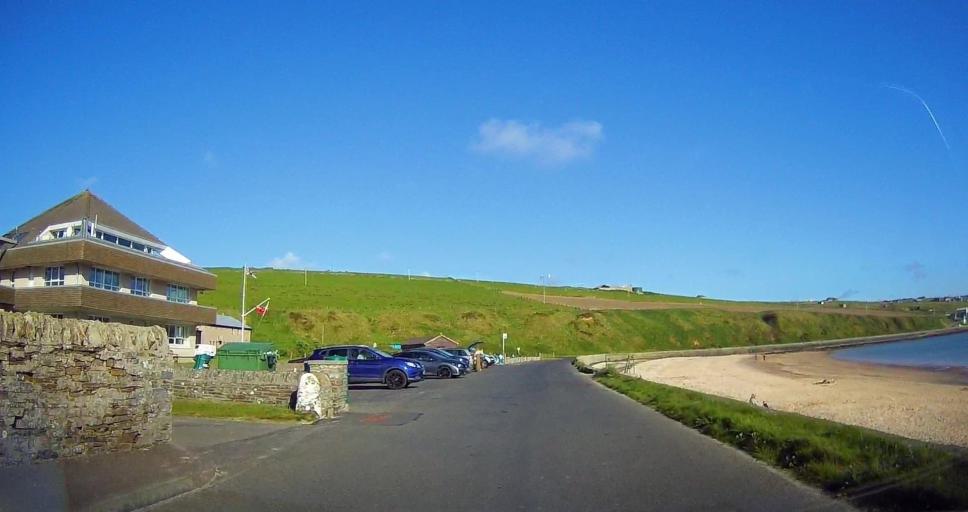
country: GB
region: Scotland
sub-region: Orkney Islands
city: Orkney
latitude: 58.9612
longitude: -2.9712
